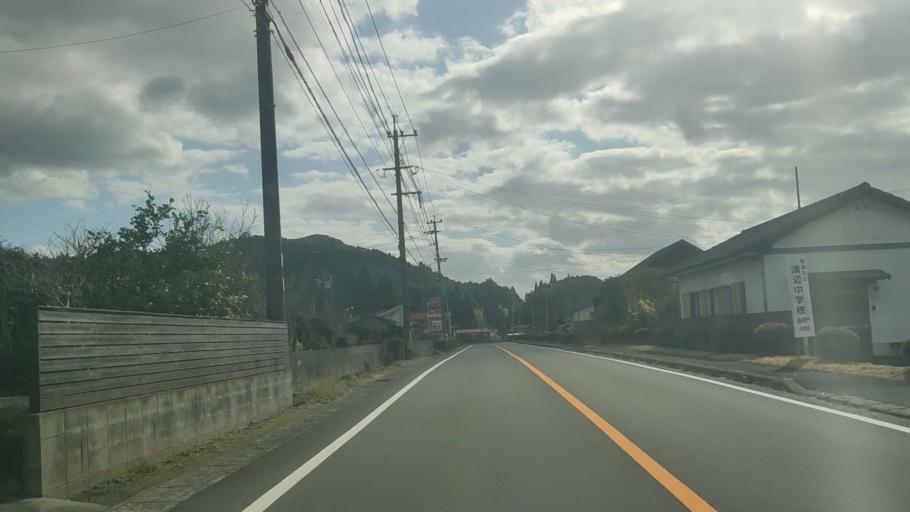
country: JP
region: Kagoshima
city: Kajiki
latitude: 31.8337
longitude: 130.6877
